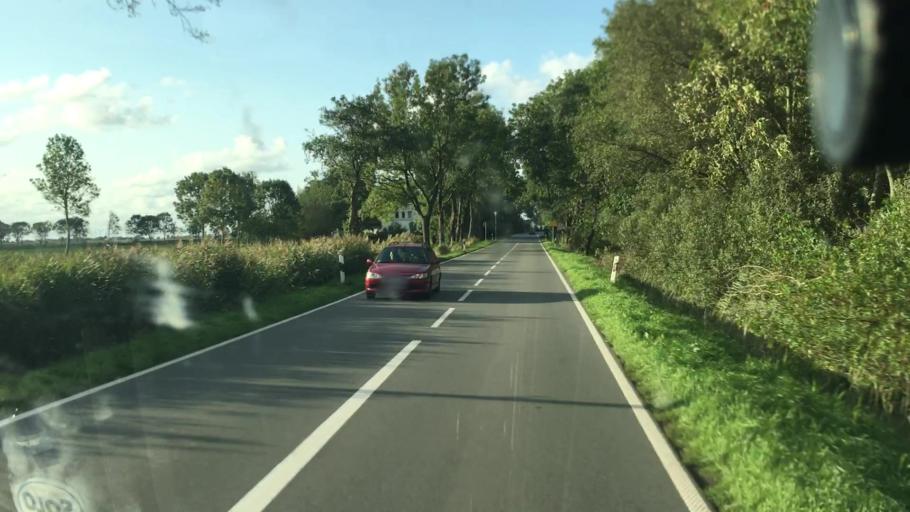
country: DE
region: Lower Saxony
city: Jever
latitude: 53.5944
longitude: 7.8696
